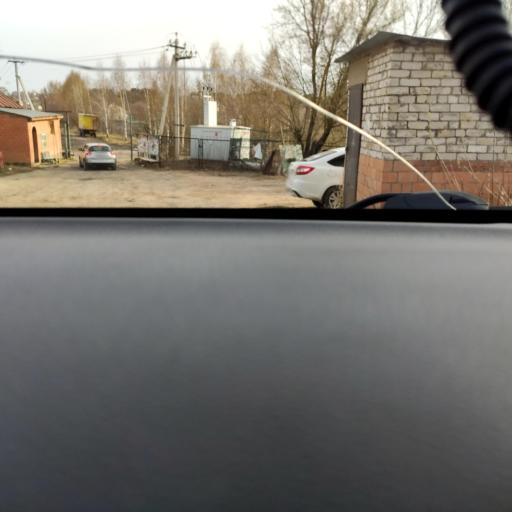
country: RU
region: Tatarstan
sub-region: Gorod Kazan'
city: Kazan
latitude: 55.8856
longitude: 49.0687
